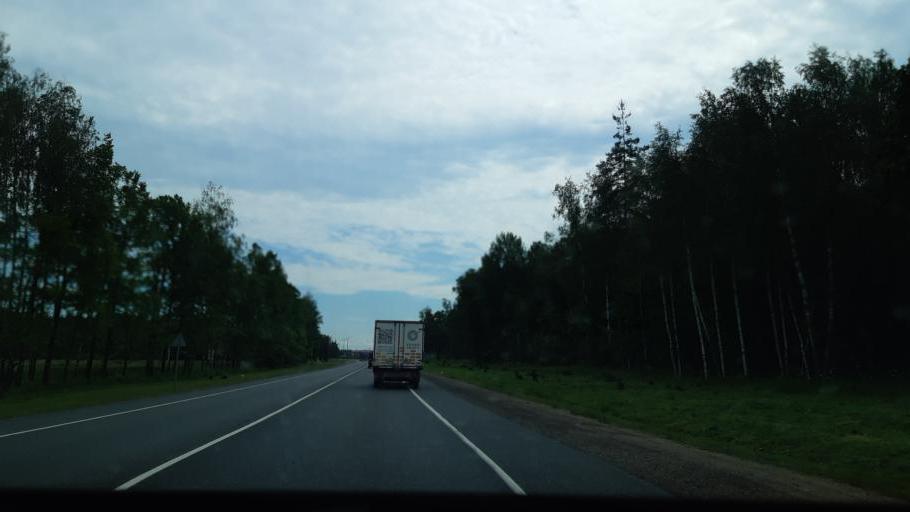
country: RU
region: Moskovskaya
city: Dorokhovo
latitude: 55.4356
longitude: 36.3517
